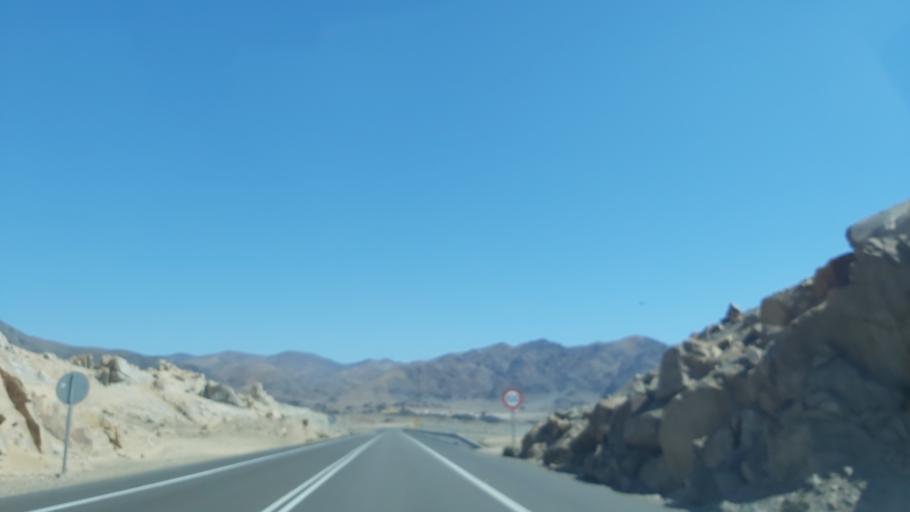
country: CL
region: Atacama
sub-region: Provincia de Chanaral
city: Diego de Almagro
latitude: -26.3804
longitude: -70.6635
